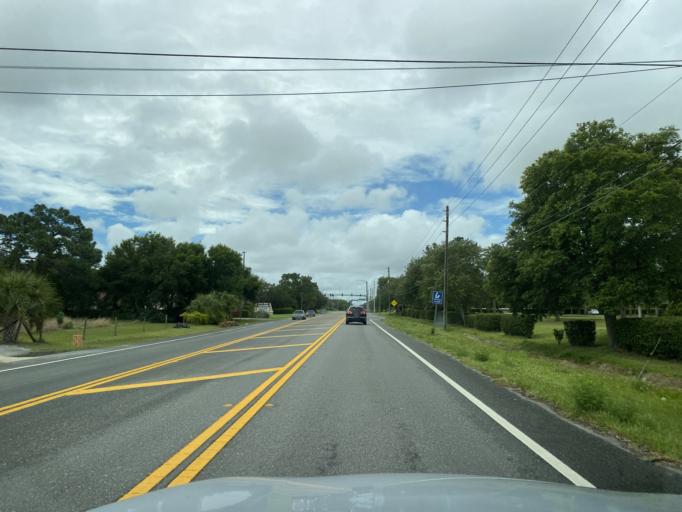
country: US
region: Florida
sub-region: Brevard County
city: West Melbourne
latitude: 28.0598
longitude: -80.6539
